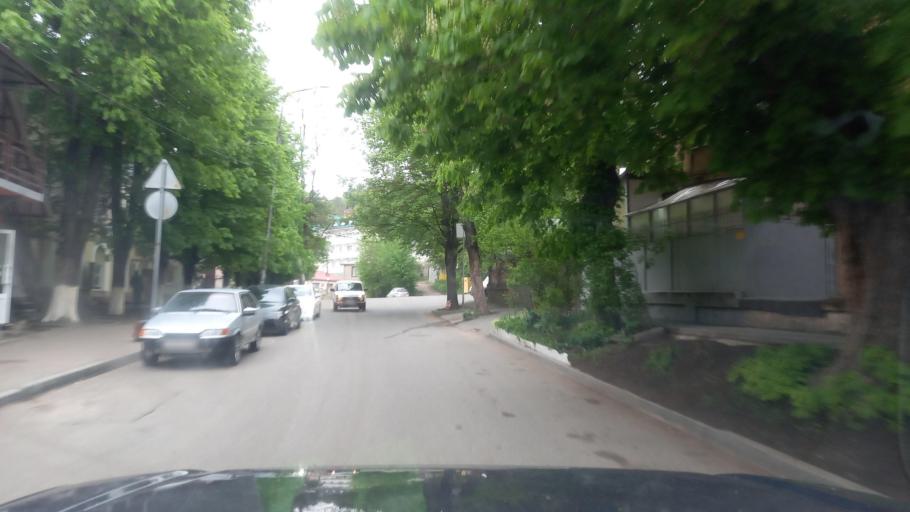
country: RU
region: Stavropol'skiy
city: Kislovodsk
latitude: 43.9024
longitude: 42.7117
